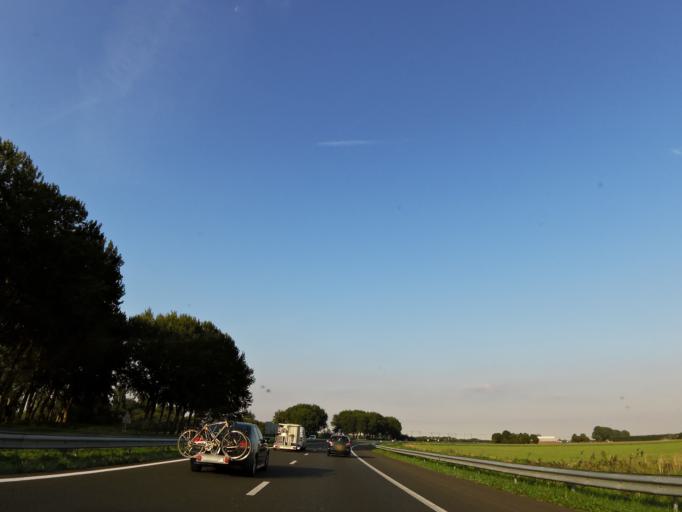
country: NL
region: Zeeland
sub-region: Gemeente Veere
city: Veere
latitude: 51.5008
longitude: 3.6848
